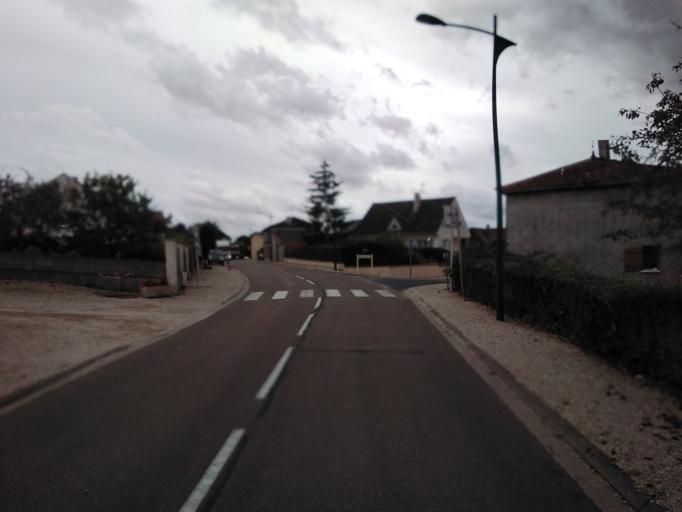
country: FR
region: Champagne-Ardenne
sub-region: Departement de la Marne
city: Frignicourt
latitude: 48.5560
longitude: 4.5229
